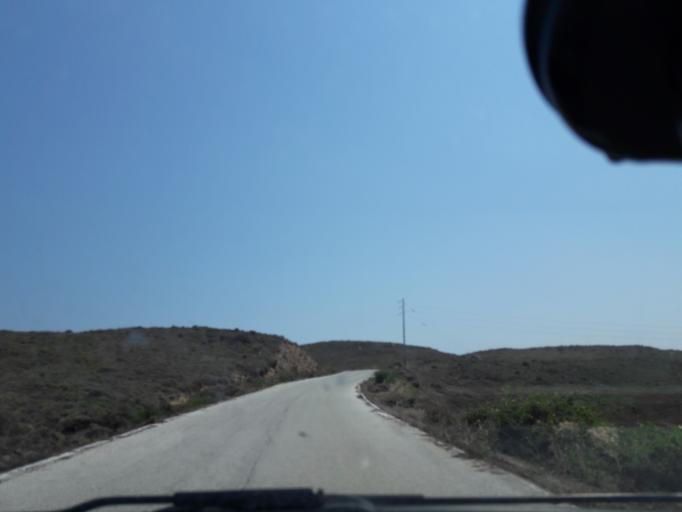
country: GR
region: North Aegean
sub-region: Nomos Lesvou
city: Myrina
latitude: 39.9768
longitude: 25.3506
